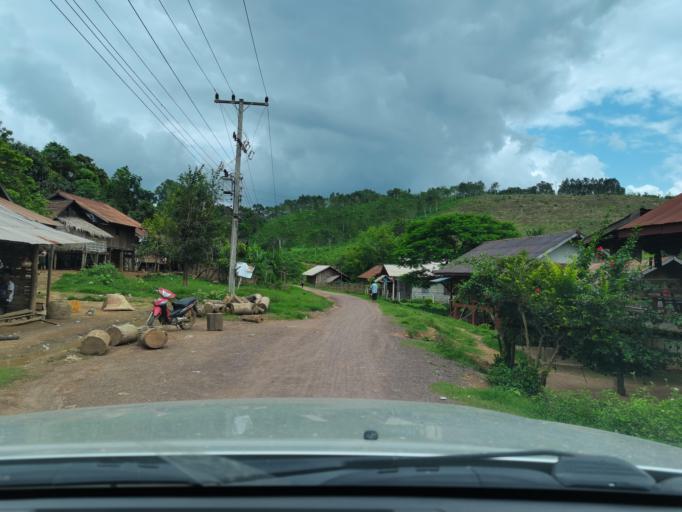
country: LA
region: Loungnamtha
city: Muang Long
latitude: 20.7055
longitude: 101.0101
